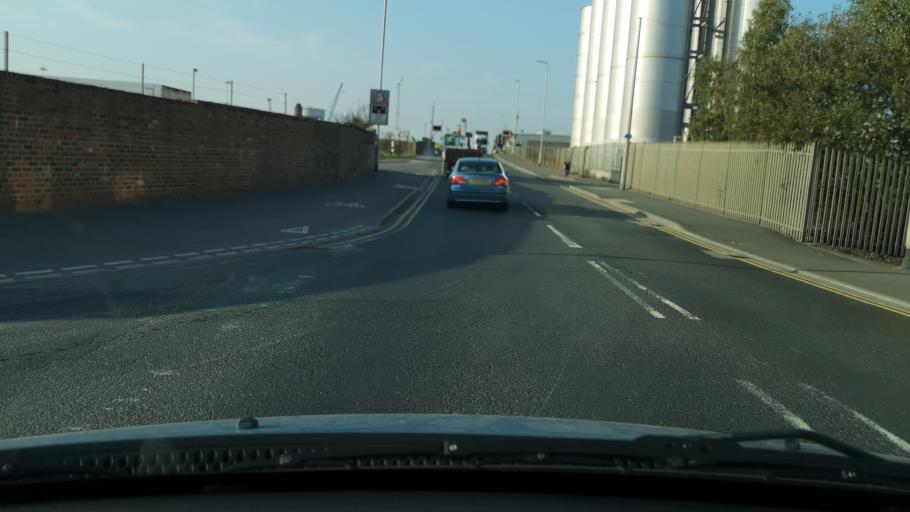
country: GB
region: England
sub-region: East Riding of Yorkshire
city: Goole
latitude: 53.6966
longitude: -0.8737
